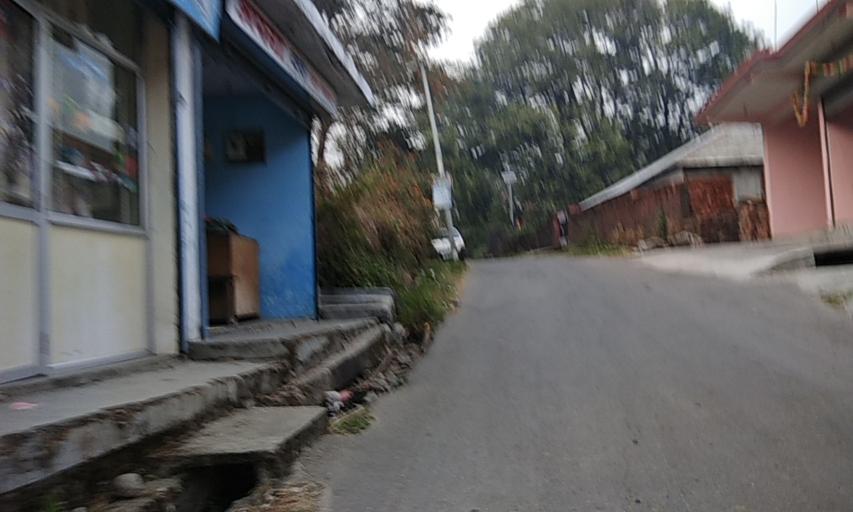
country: IN
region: Himachal Pradesh
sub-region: Kangra
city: Palampur
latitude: 32.1181
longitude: 76.5329
